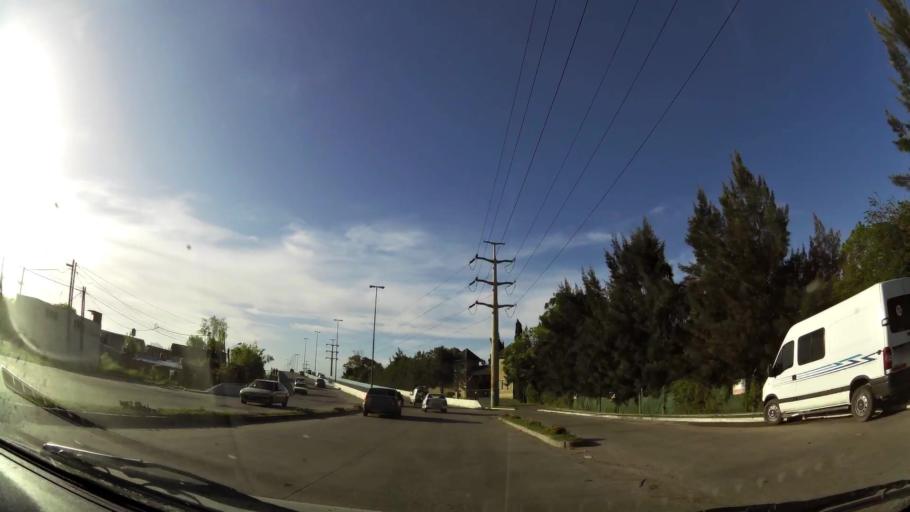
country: AR
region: Buenos Aires
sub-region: Partido de Quilmes
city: Quilmes
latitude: -34.8021
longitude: -58.2079
